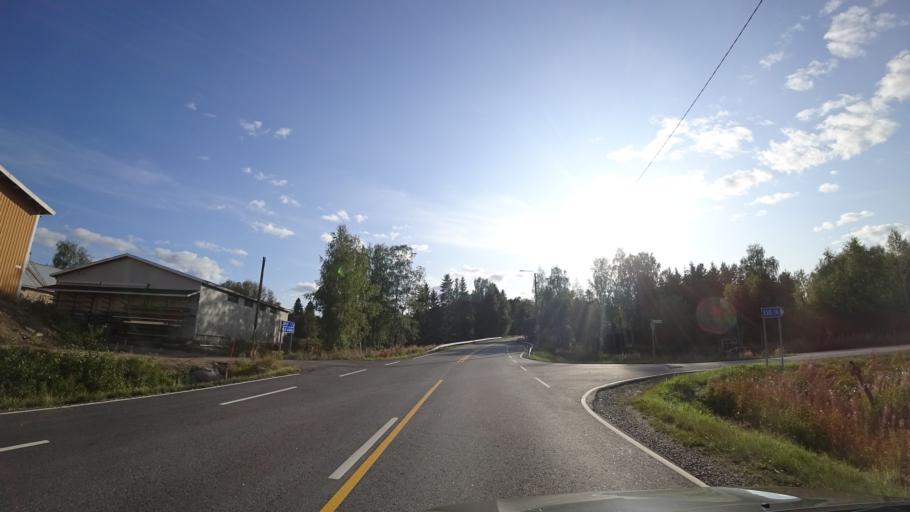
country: FI
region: Paijanne Tavastia
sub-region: Lahti
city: Hollola
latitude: 61.1409
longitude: 25.3277
